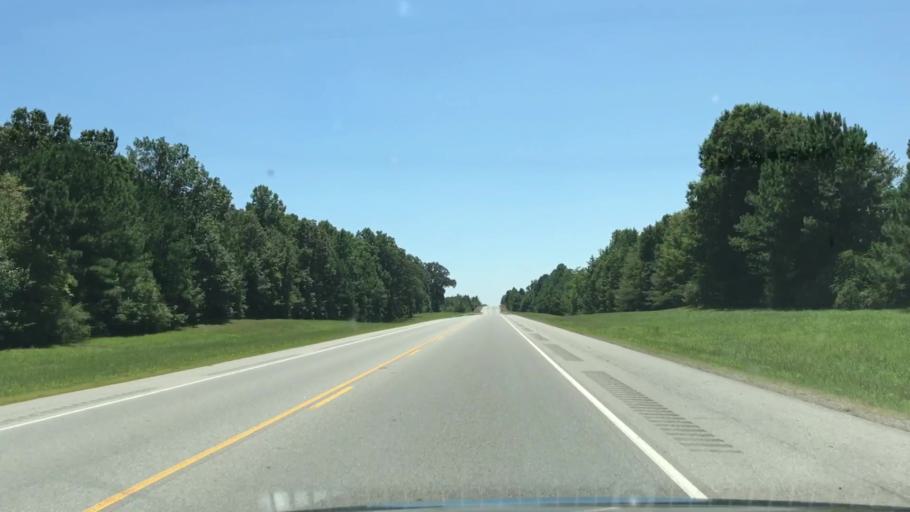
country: US
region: Tennessee
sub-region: Putnam County
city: Baxter
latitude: 36.1673
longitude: -85.6279
